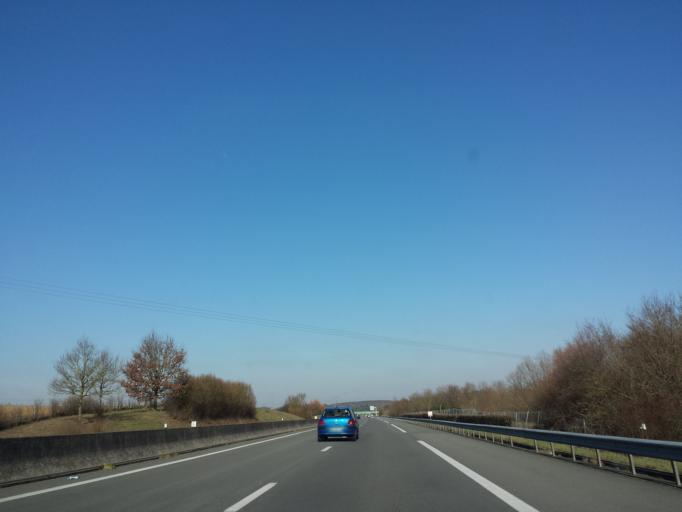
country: FR
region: Picardie
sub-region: Departement de la Somme
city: Conty
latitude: 49.7278
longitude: 2.2384
